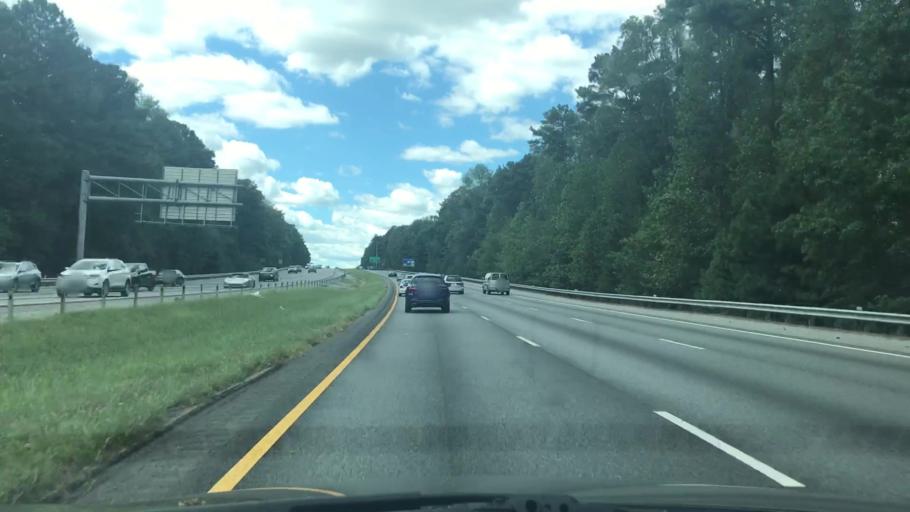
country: US
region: Georgia
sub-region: DeKalb County
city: Stone Mountain
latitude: 33.8315
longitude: -84.1834
